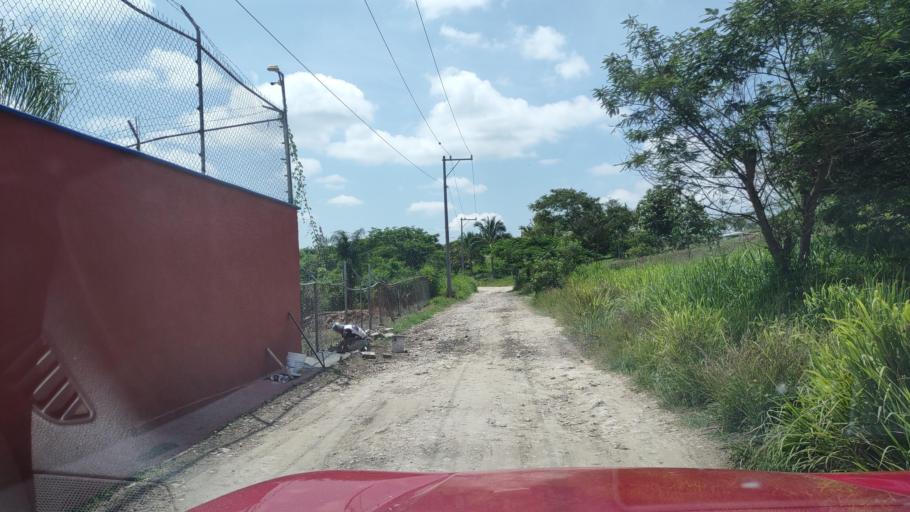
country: MX
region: Veracruz
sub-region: Emiliano Zapata
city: Dos Rios
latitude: 19.4630
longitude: -96.7907
